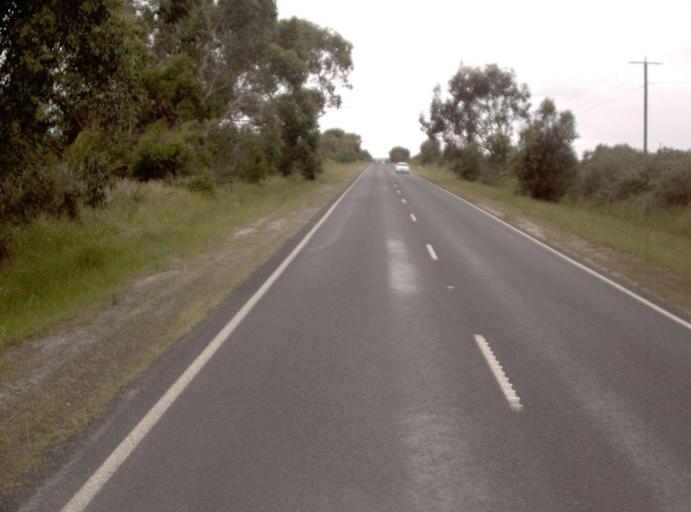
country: AU
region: Victoria
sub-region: Baw Baw
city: Warragul
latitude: -38.5797
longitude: 146.0439
